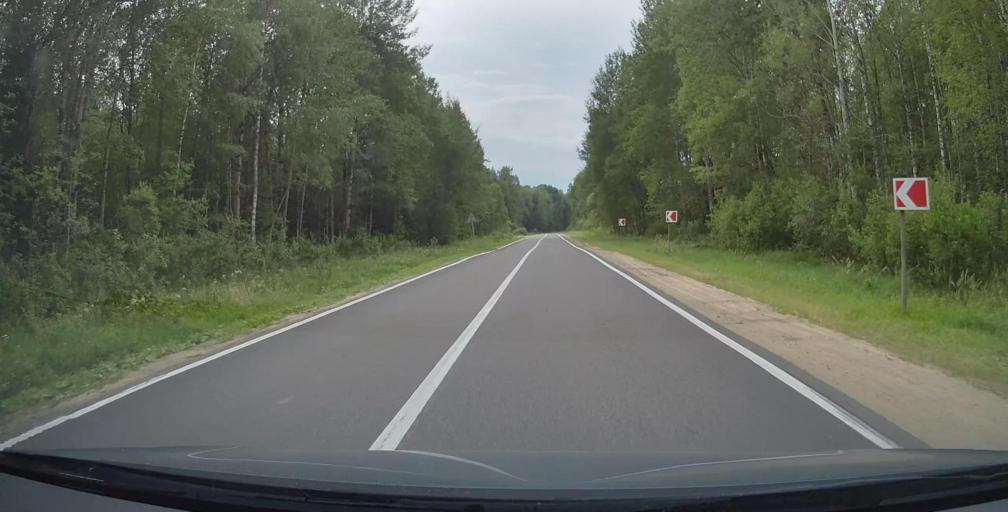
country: RU
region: Jaroslavl
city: Rybinsk
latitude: 57.9374
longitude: 38.6780
